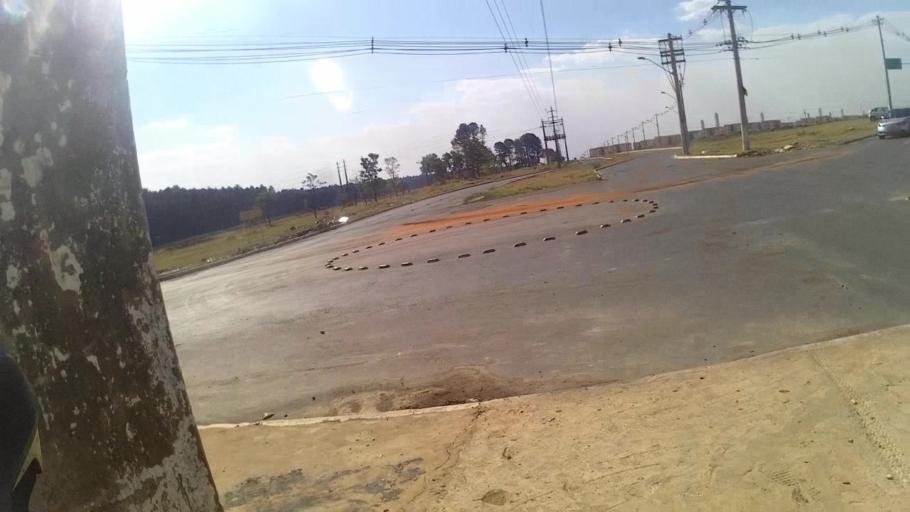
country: BR
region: Federal District
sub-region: Brasilia
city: Brasilia
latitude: -15.7762
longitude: -47.7839
